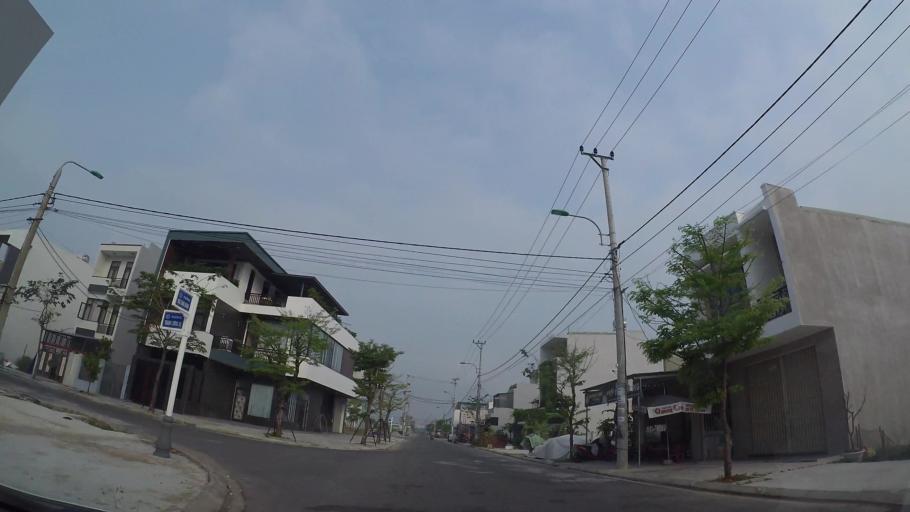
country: VN
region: Da Nang
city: Cam Le
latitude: 16.0151
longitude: 108.2211
